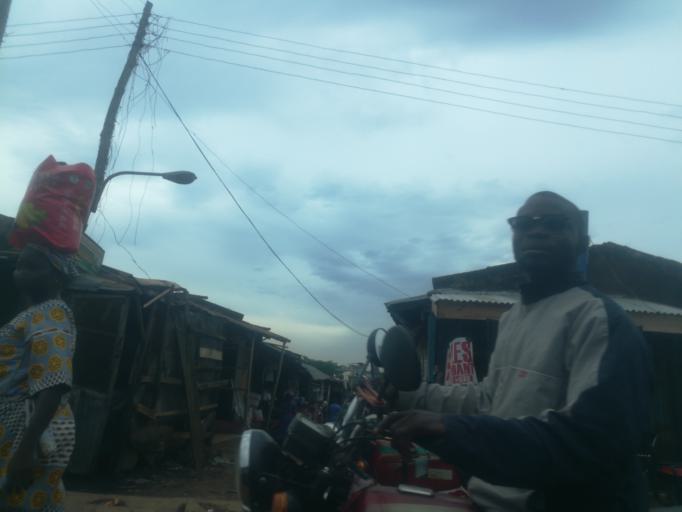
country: NG
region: Oyo
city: Egbeda
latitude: 7.3816
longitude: 3.9943
